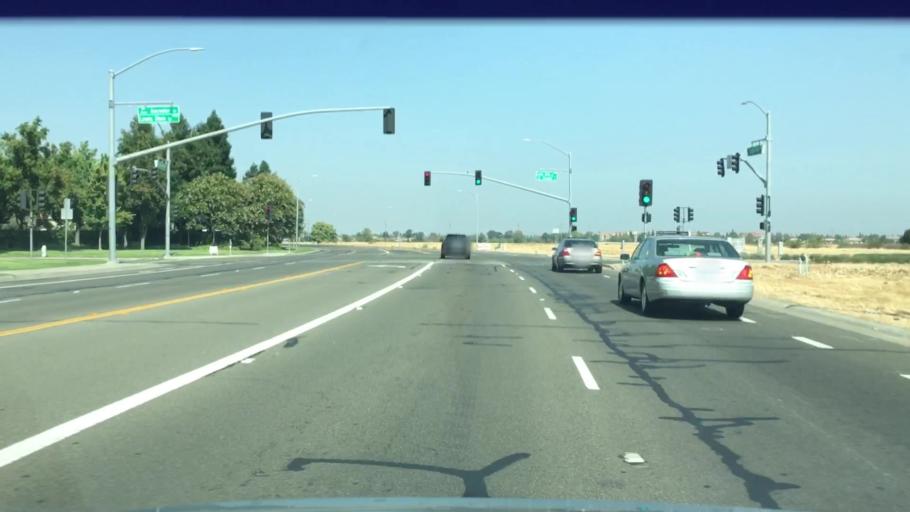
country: US
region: California
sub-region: Sacramento County
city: Laguna
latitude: 38.4289
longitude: -121.4117
